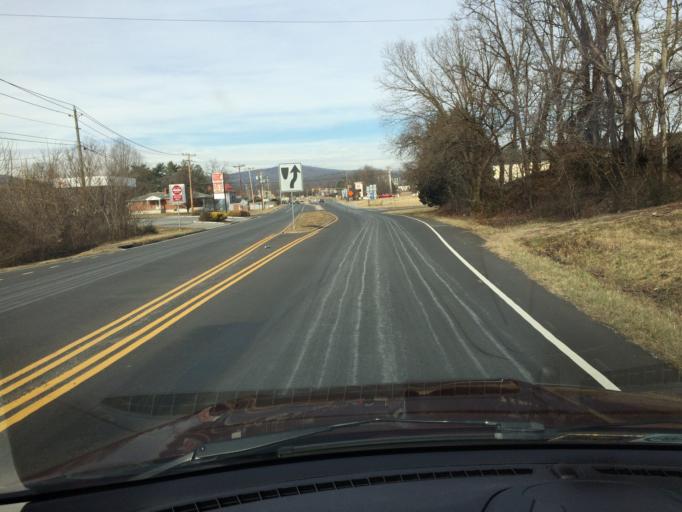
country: US
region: Virginia
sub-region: Roanoke County
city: Hollins
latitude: 37.3461
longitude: -79.9491
